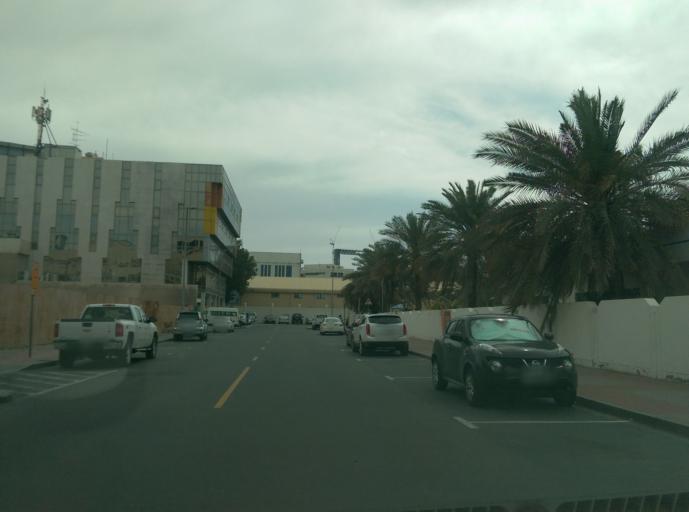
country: AE
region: Ash Shariqah
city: Sharjah
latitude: 25.2446
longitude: 55.3102
